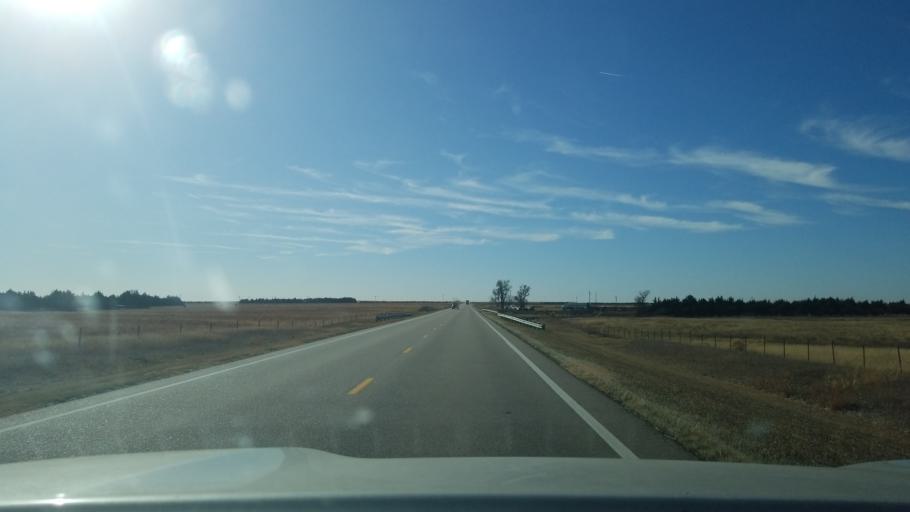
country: US
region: Kansas
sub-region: Ness County
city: Ness City
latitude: 38.3698
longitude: -99.8980
